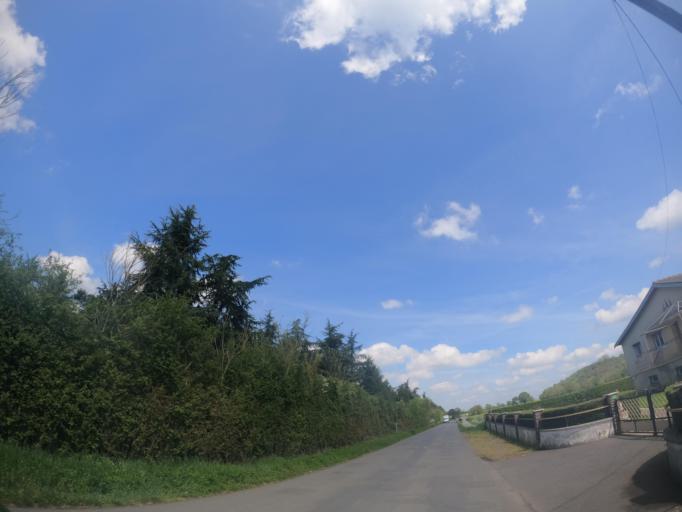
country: FR
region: Poitou-Charentes
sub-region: Departement des Deux-Sevres
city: Saint-Varent
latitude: 46.8654
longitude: -0.2458
